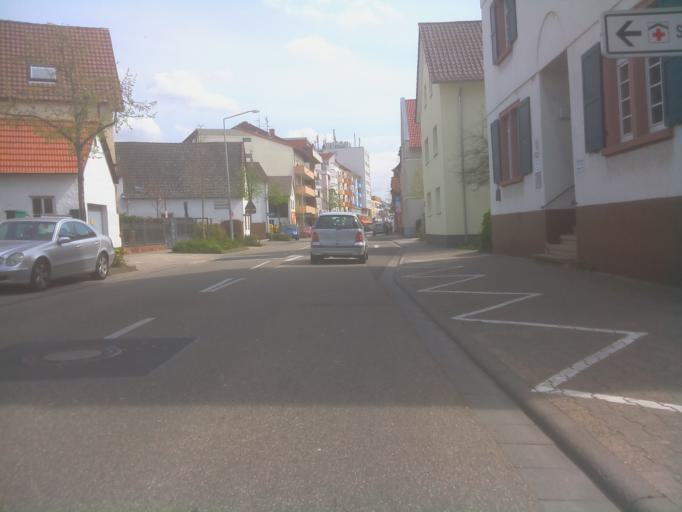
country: DE
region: Hesse
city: Lampertheim
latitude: 49.5960
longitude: 8.4663
